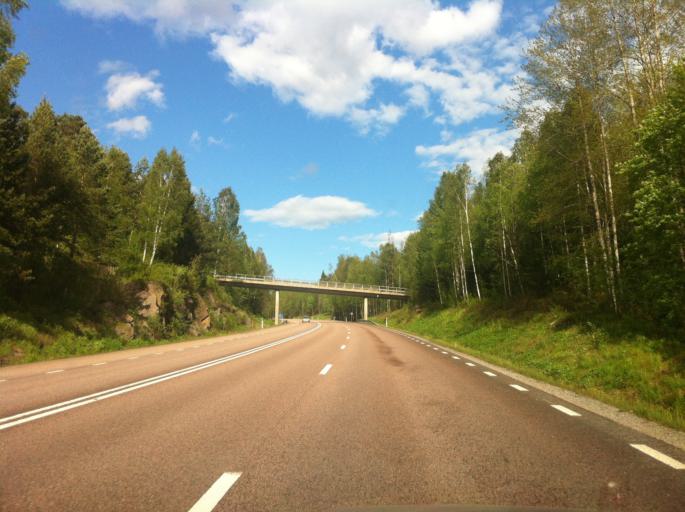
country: SE
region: Vaermland
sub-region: Filipstads Kommun
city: Filipstad
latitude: 59.7127
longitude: 14.1762
